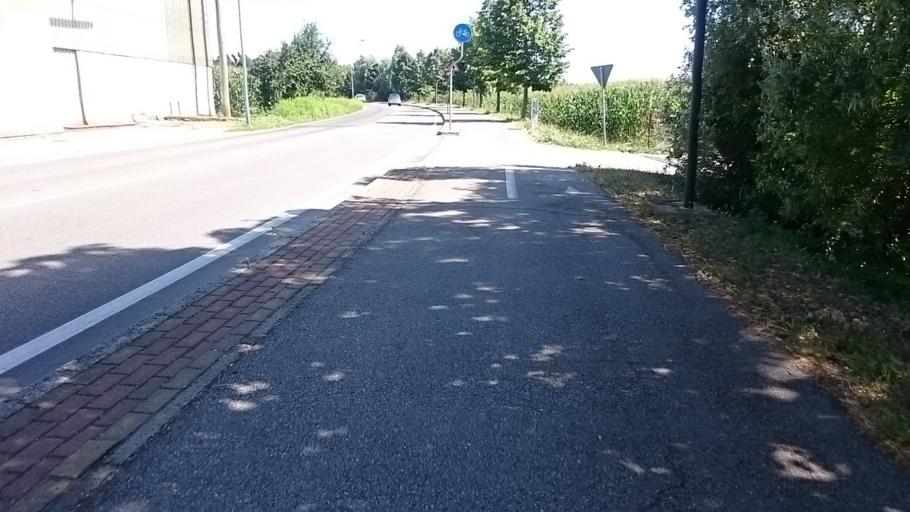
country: IT
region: Veneto
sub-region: Provincia di Venezia
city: Arino
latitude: 45.4309
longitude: 12.0522
